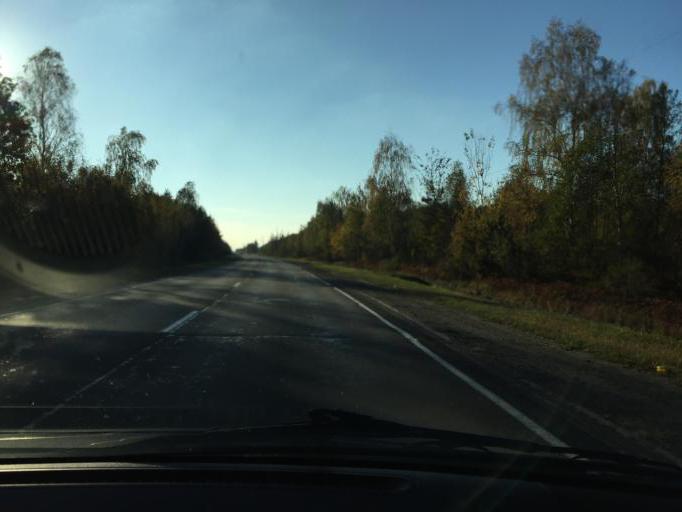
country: BY
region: Brest
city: Horad Luninyets
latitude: 52.3181
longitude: 26.5833
